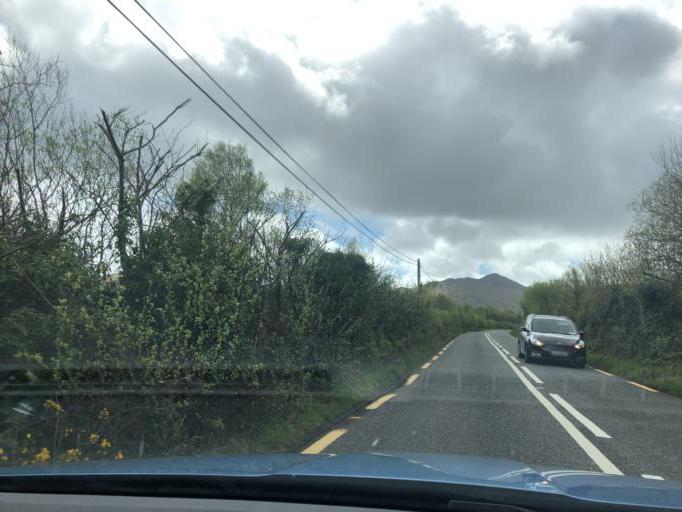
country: IE
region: Munster
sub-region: Ciarrai
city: Killorglin
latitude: 51.8352
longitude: -9.9197
